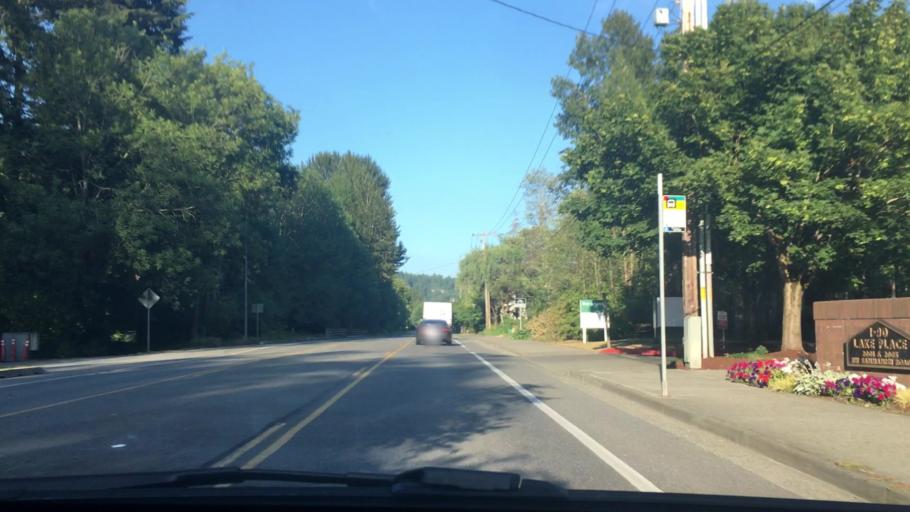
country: US
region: Washington
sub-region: King County
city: Issaquah
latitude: 47.5519
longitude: -122.0654
